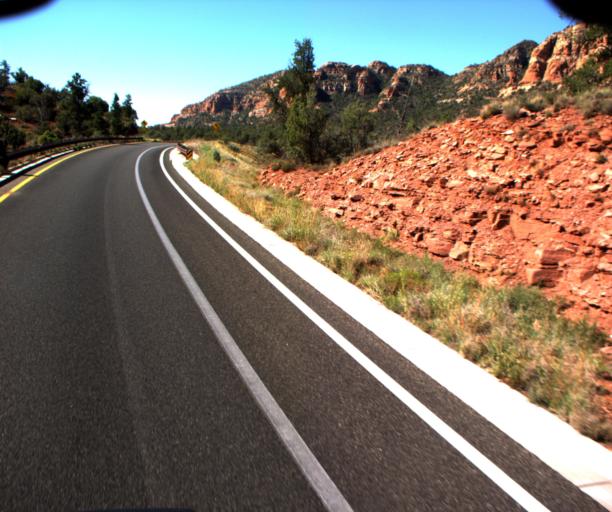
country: US
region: Arizona
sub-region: Yavapai County
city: Village of Oak Creek (Big Park)
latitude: 34.8134
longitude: -111.7688
